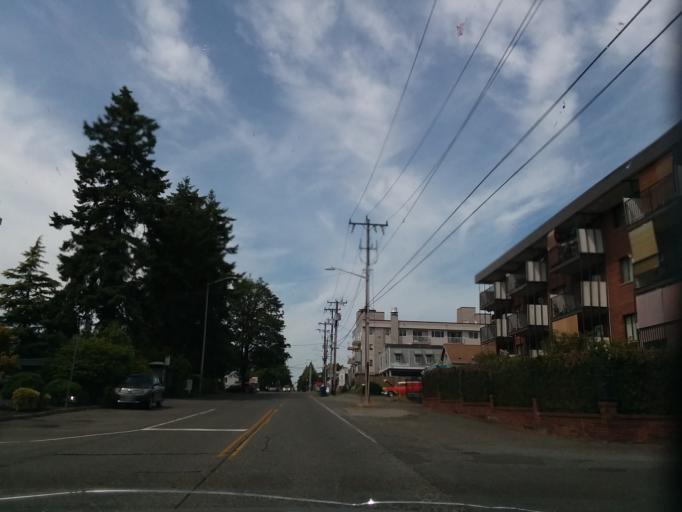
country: US
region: Washington
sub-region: King County
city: Shoreline
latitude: 47.7122
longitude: -122.3124
